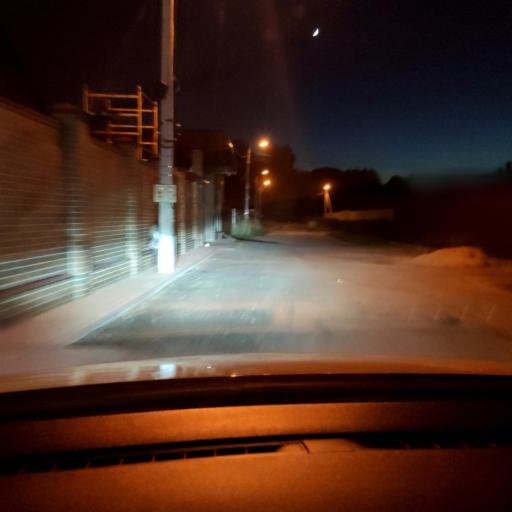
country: RU
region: Voronezj
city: Pridonskoy
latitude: 51.6457
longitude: 39.0912
